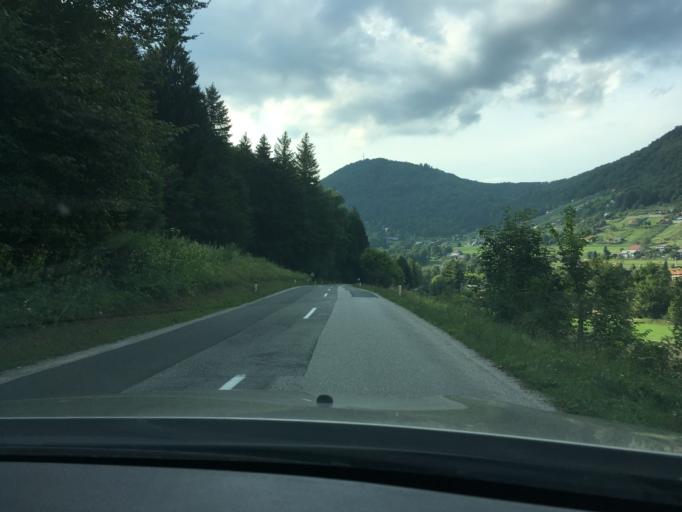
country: SI
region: Dolenjske Toplice
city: Dolenjske Toplice
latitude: 45.7760
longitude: 15.0214
